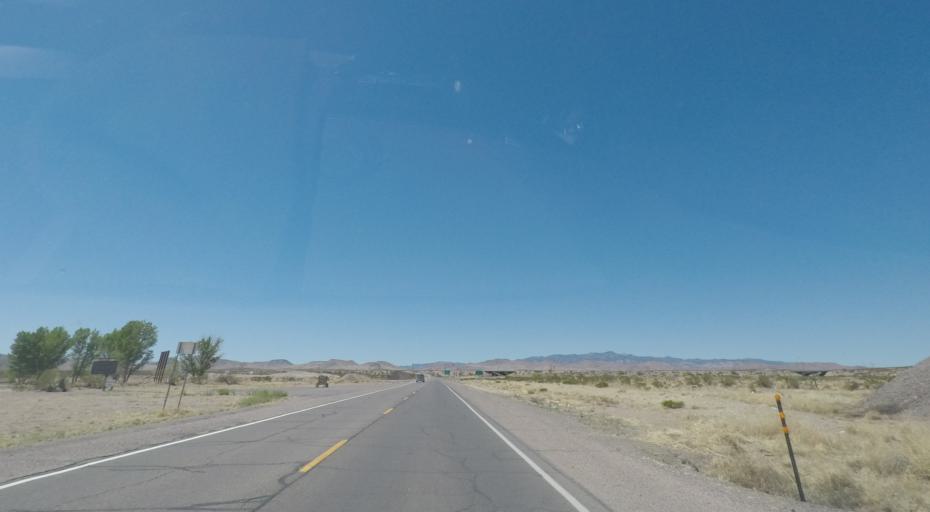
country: US
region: New Mexico
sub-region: Socorro County
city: Socorro
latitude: 33.9175
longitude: -106.8725
